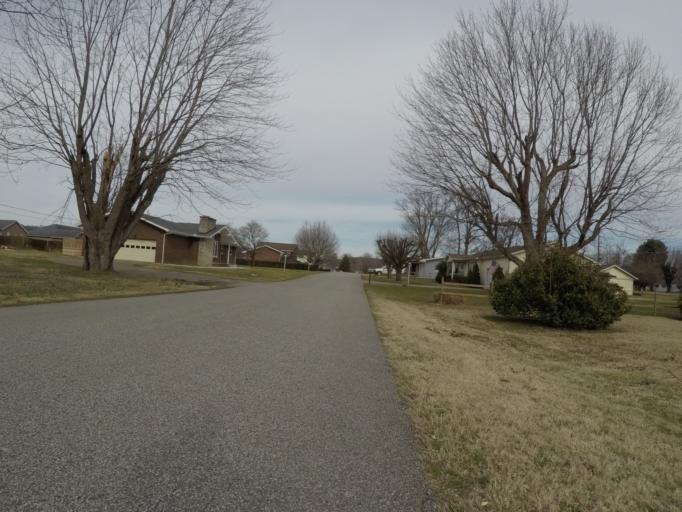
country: US
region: West Virginia
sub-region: Cabell County
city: Pea Ridge
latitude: 38.4434
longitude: -82.3477
